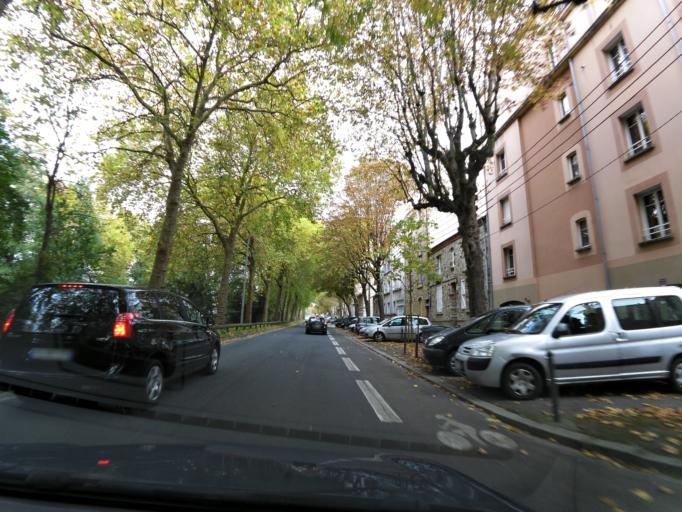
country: FR
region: Brittany
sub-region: Departement d'Ille-et-Vilaine
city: Rennes
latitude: 48.1159
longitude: -1.6868
